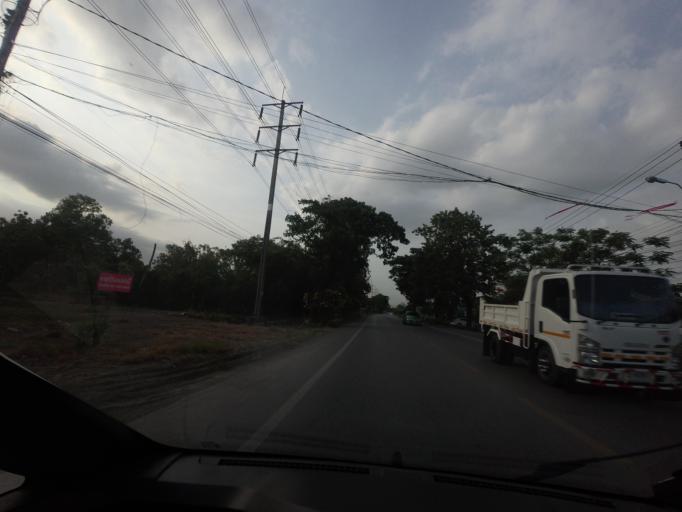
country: TH
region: Bangkok
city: Nong Chok
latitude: 13.8722
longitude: 100.8631
